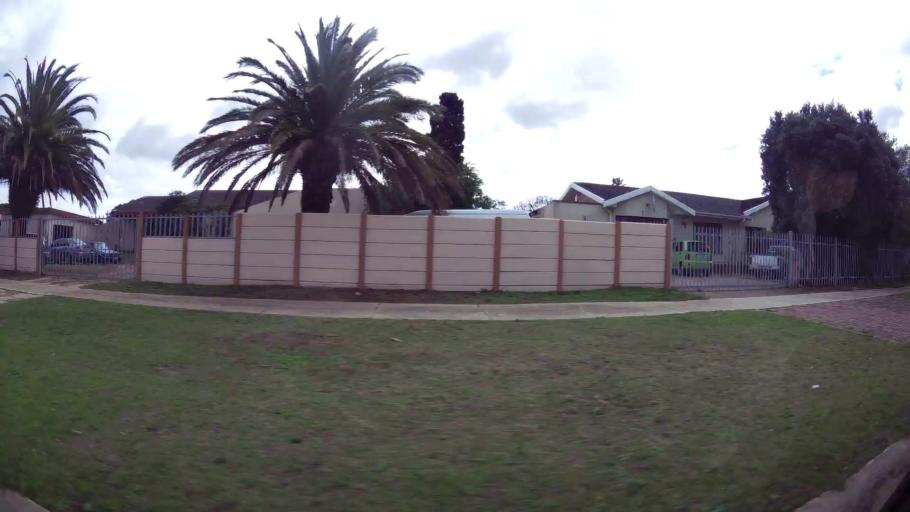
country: ZA
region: Eastern Cape
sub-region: Nelson Mandela Bay Metropolitan Municipality
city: Port Elizabeth
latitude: -33.9344
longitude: 25.5256
